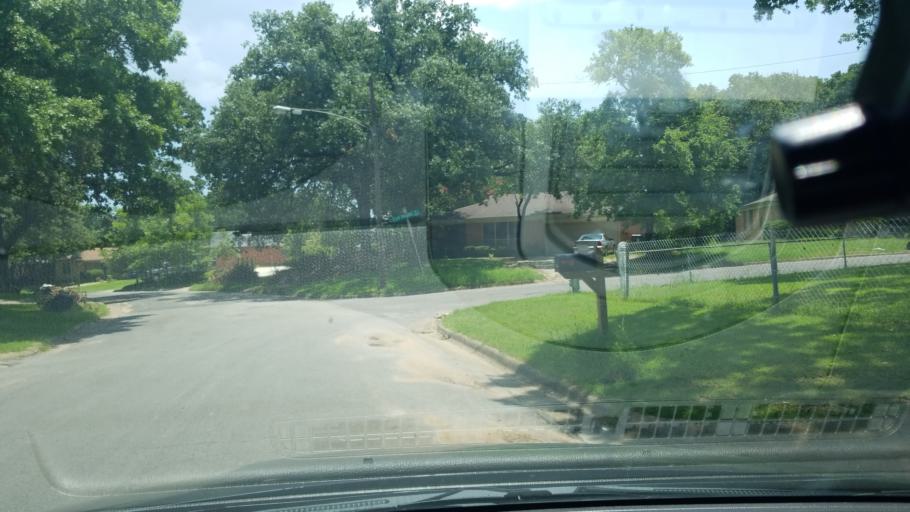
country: US
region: Texas
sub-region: Dallas County
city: Balch Springs
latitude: 32.7212
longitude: -96.6707
